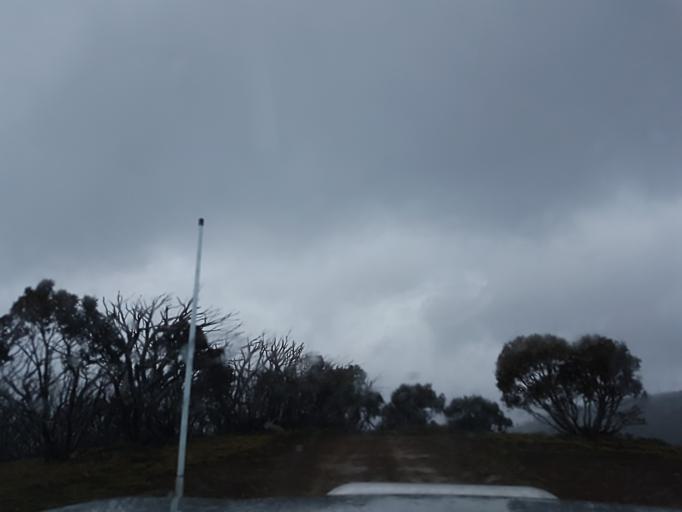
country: AU
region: Victoria
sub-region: Alpine
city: Mount Beauty
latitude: -37.0943
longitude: 147.0587
